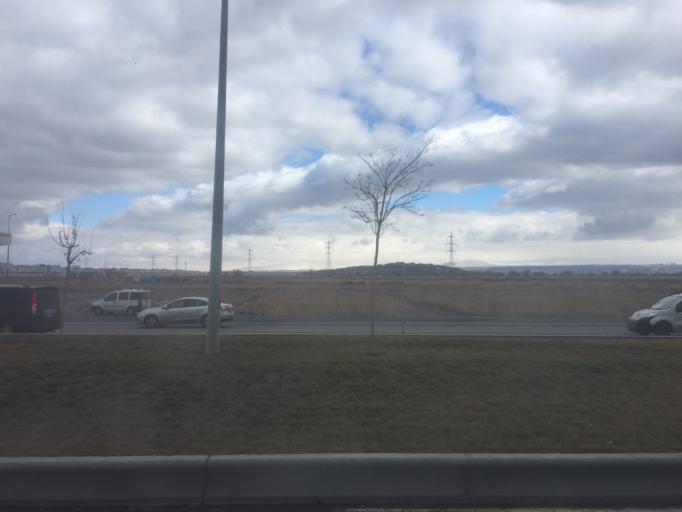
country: TR
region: Kayseri
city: Melikgazi
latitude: 38.7686
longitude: 35.4124
